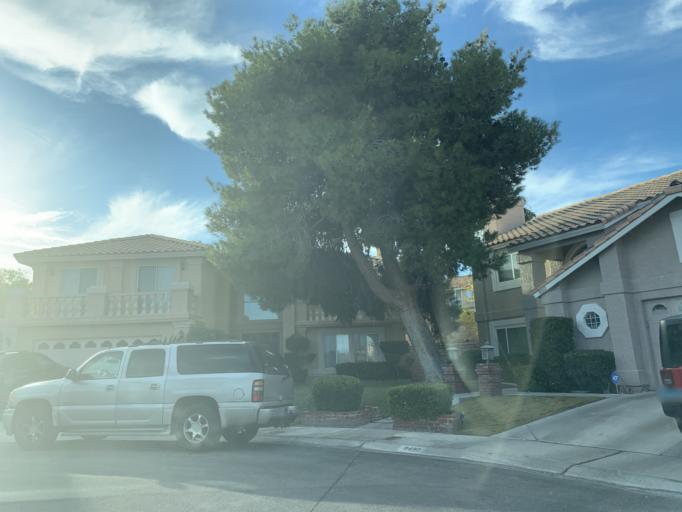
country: US
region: Nevada
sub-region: Clark County
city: Summerlin South
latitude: 36.1347
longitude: -115.2997
